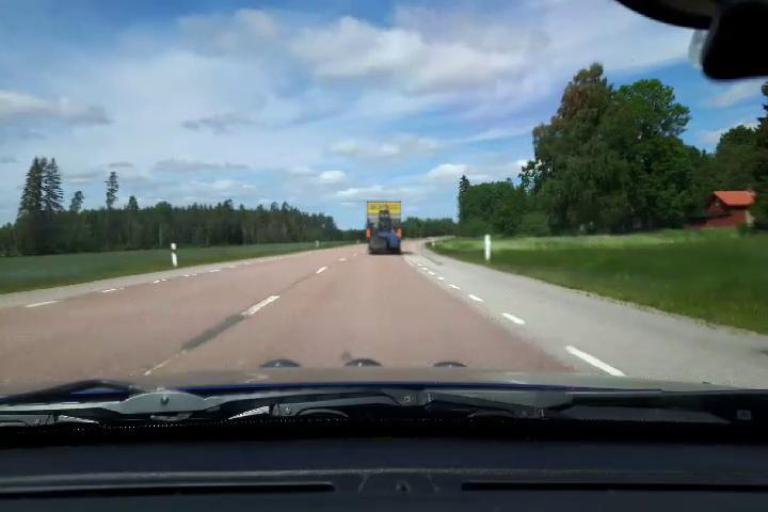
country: SE
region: Uppsala
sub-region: Osthammars Kommun
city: Bjorklinge
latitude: 60.1550
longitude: 17.4912
